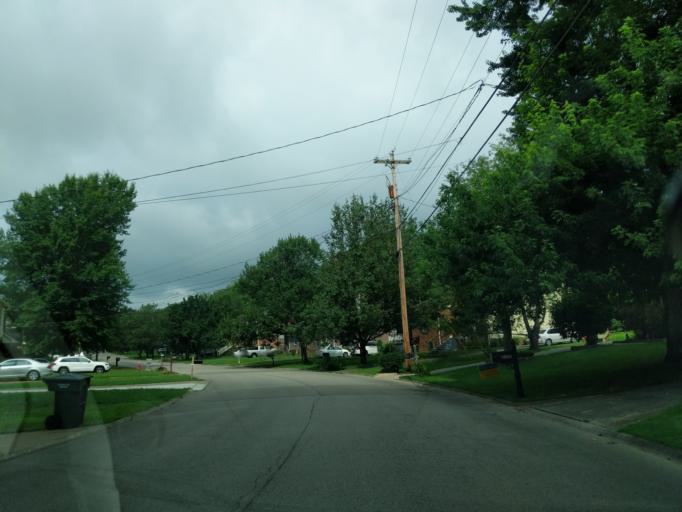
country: US
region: Tennessee
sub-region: Davidson County
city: Lakewood
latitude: 36.1765
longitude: -86.6188
